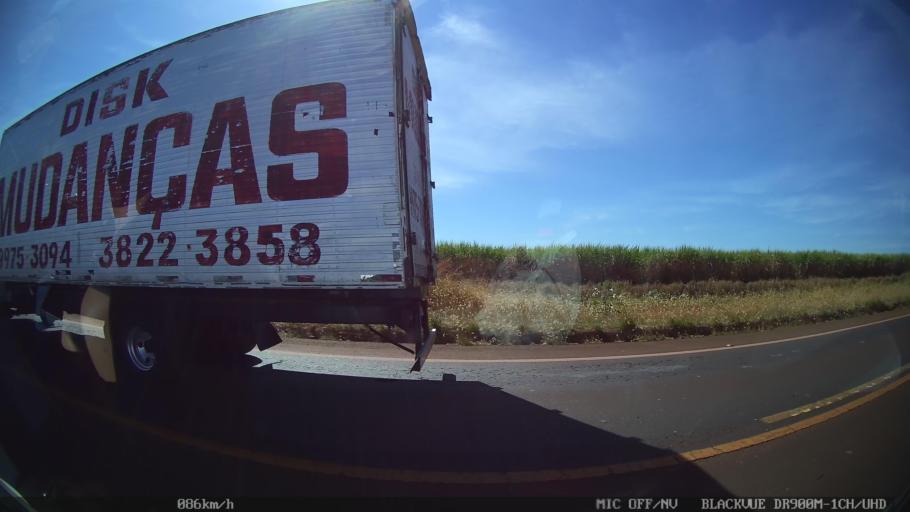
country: BR
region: Sao Paulo
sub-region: Ipua
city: Ipua
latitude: -20.4769
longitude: -48.0896
